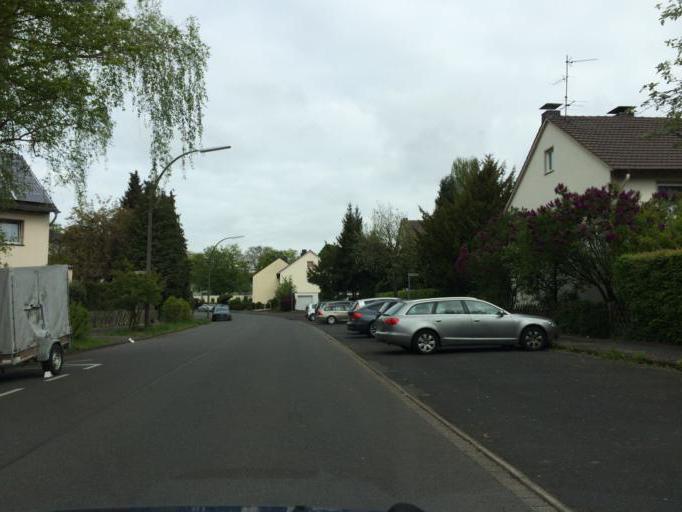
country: DE
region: North Rhine-Westphalia
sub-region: Regierungsbezirk Koln
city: Konigswinter
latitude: 50.6687
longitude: 7.1695
